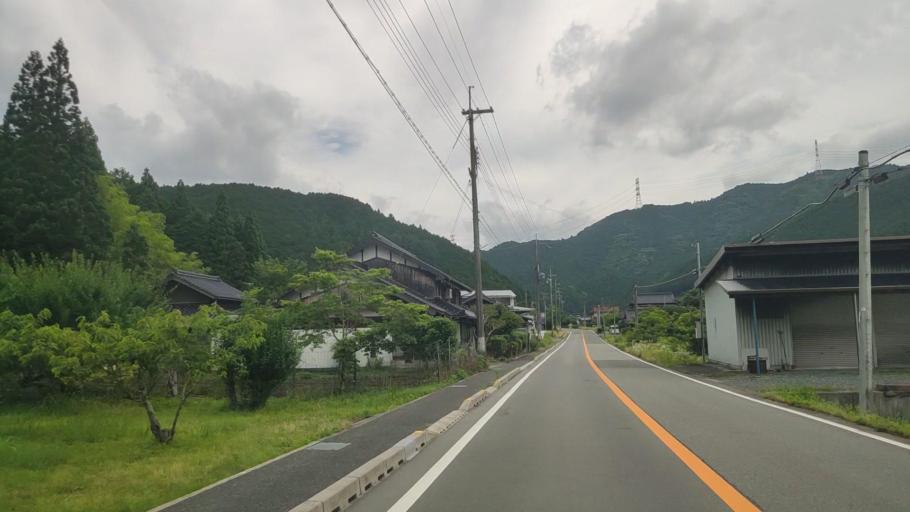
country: JP
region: Kyoto
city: Fukuchiyama
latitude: 35.2763
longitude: 134.9848
